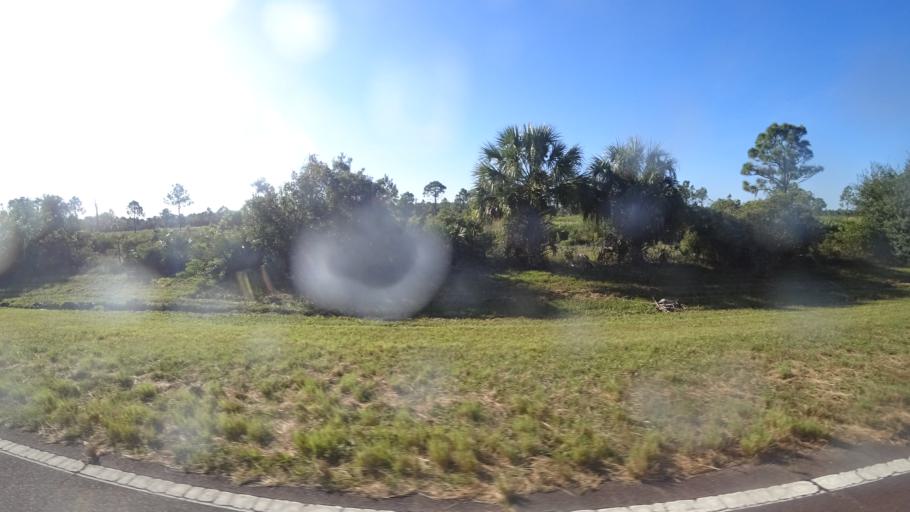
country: US
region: Florida
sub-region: Hillsborough County
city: Ruskin
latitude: 27.6538
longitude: -82.4775
